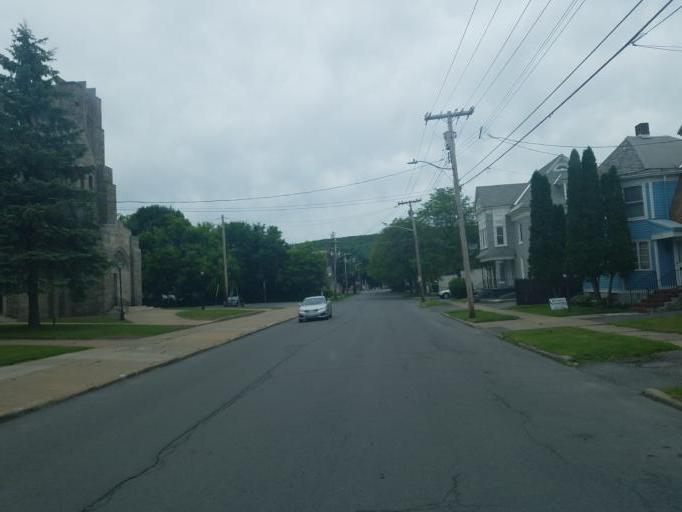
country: US
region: New York
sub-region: Herkimer County
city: Ilion
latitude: 43.0143
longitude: -75.0391
